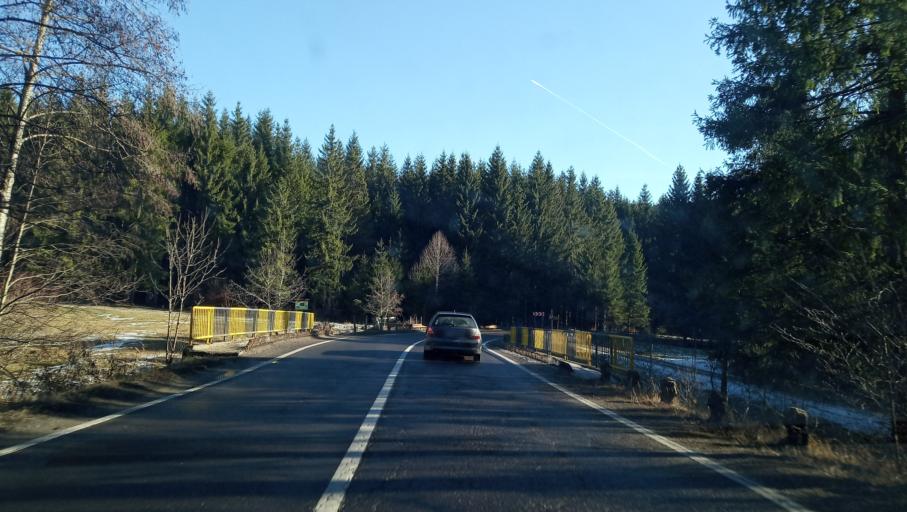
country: RO
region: Brasov
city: Crivina
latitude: 45.4611
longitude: 25.9517
